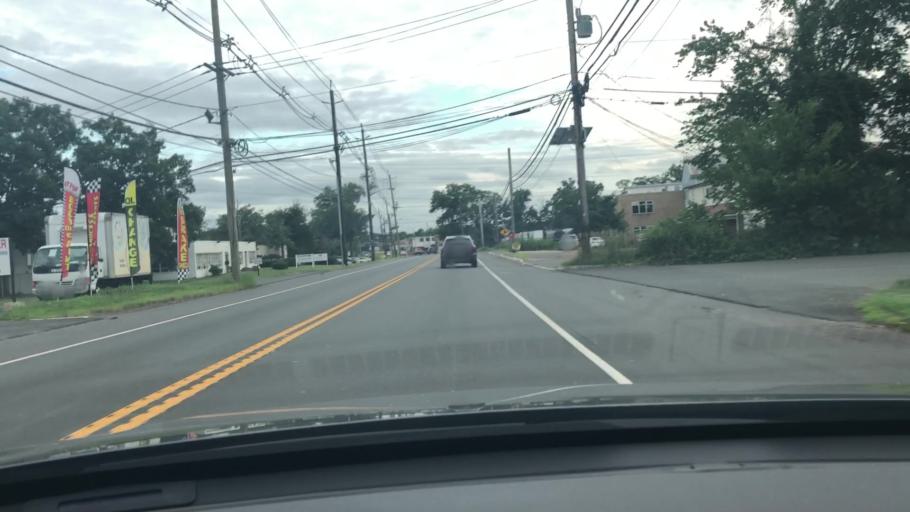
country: US
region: New Jersey
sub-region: Somerset County
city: Somerset
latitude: 40.4634
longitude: -74.4825
